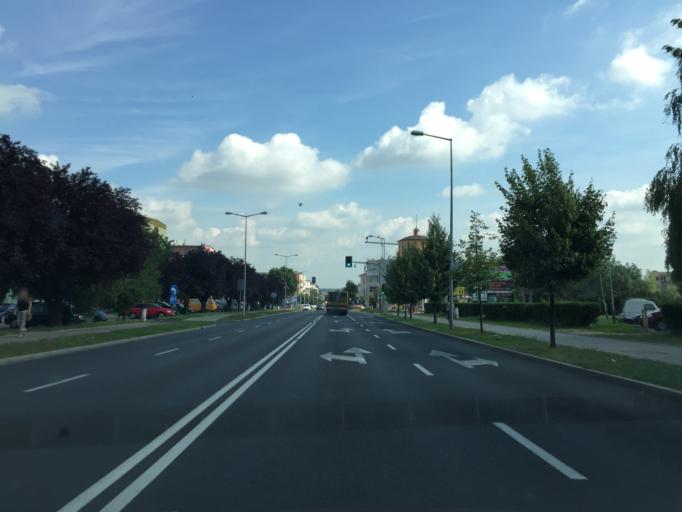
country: PL
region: Greater Poland Voivodeship
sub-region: Kalisz
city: Kalisz
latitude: 51.7488
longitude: 18.0738
